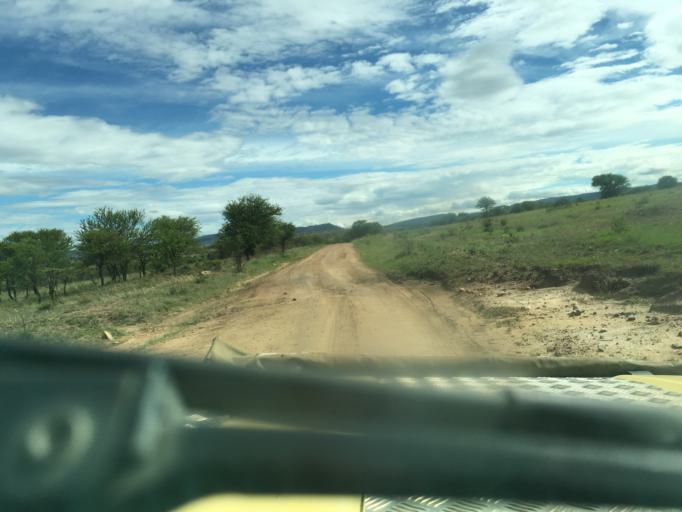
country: TZ
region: Mara
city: Mugumu
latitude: -1.9200
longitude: 35.1836
